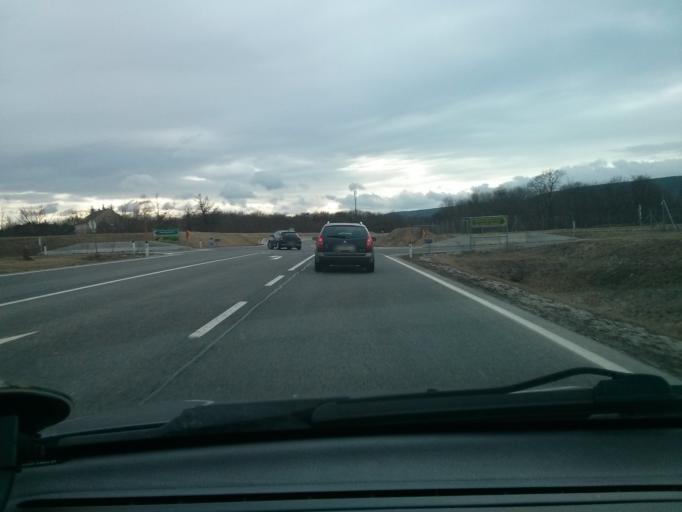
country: AT
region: Lower Austria
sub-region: Politischer Bezirk Wiener Neustadt
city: Theresienfeld
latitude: 47.8502
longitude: 16.2052
